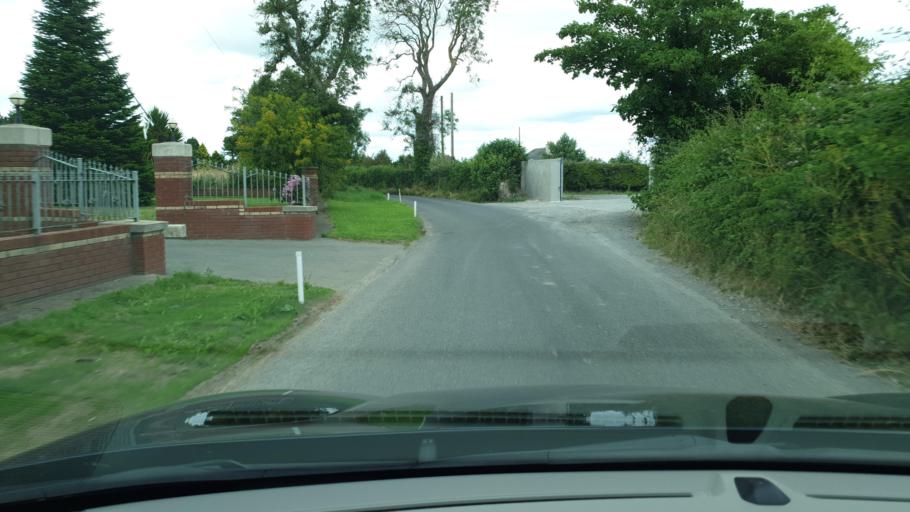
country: IE
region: Leinster
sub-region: An Mhi
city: Ashbourne
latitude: 53.4741
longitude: -6.3749
